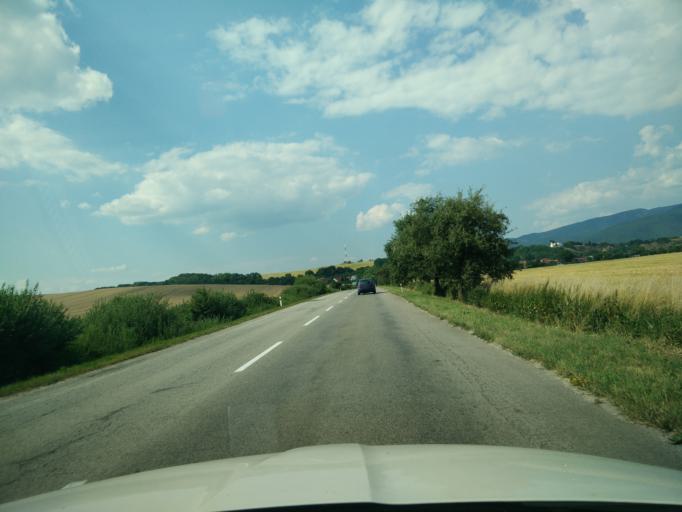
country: SK
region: Nitriansky
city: Partizanske
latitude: 48.6727
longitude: 18.3693
